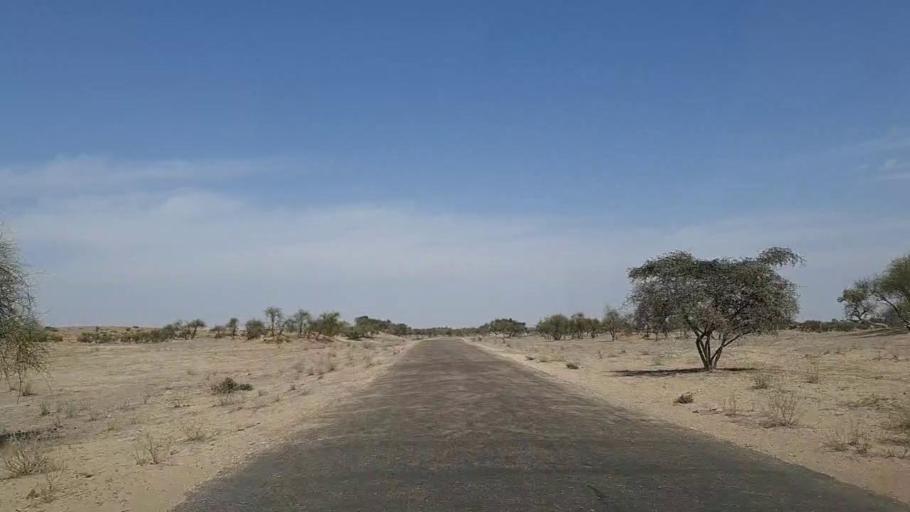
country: PK
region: Sindh
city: Nabisar
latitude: 25.0661
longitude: 69.9684
